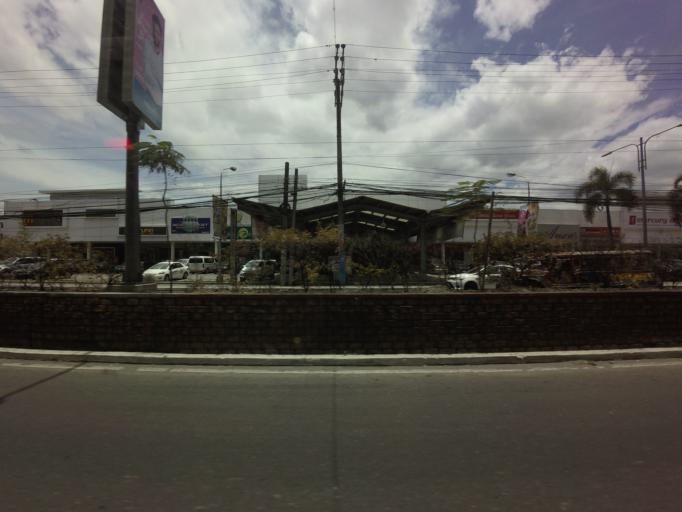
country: PH
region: Metro Manila
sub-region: Marikina
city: Calumpang
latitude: 14.6196
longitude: 121.1018
